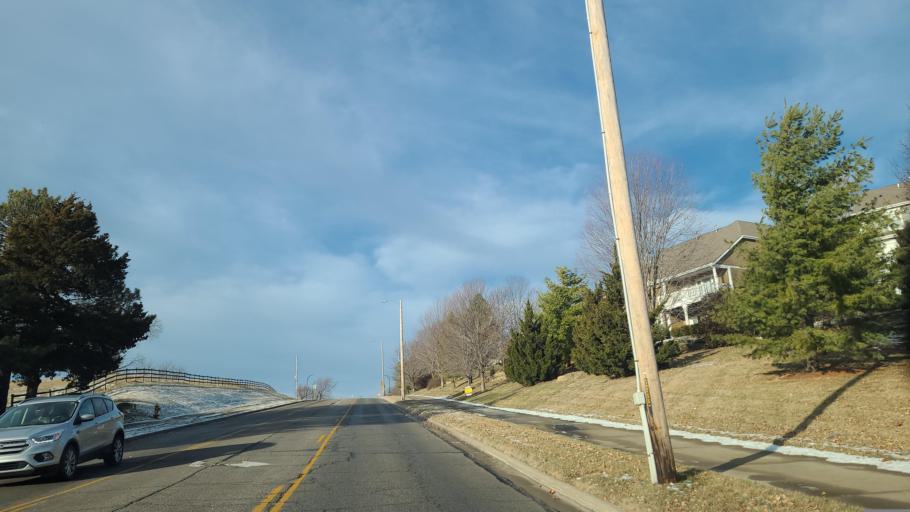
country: US
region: Kansas
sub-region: Douglas County
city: Lawrence
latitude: 38.9863
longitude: -95.2857
